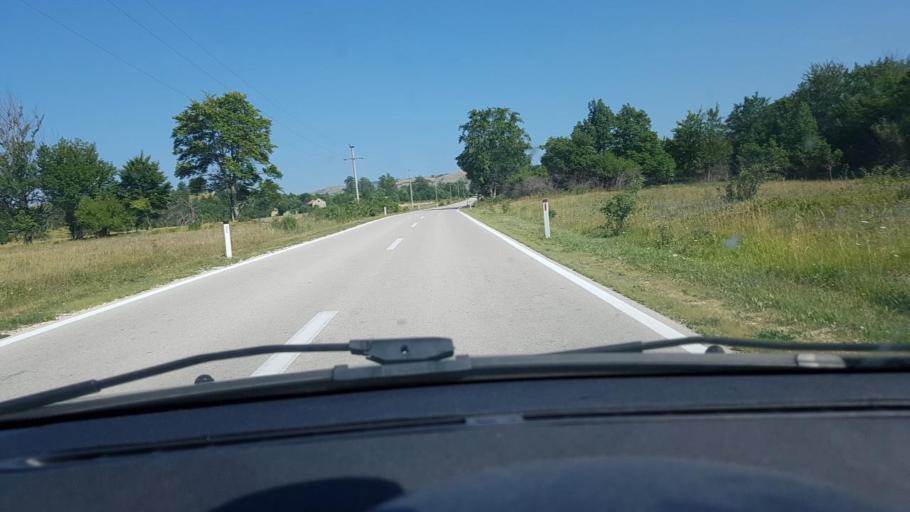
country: BA
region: Federation of Bosnia and Herzegovina
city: Bosansko Grahovo
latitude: 44.1033
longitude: 16.5507
